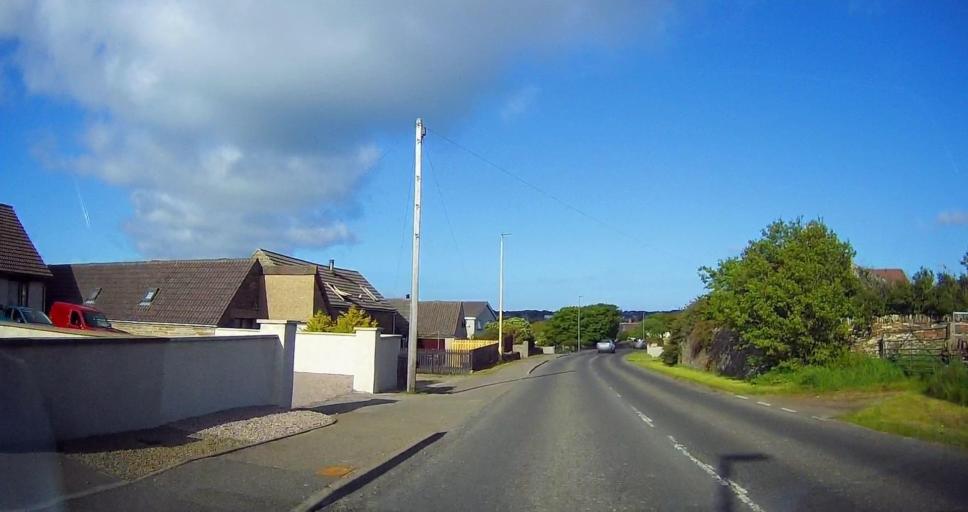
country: GB
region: Scotland
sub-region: Orkney Islands
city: Orkney
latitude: 58.9779
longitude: -2.9772
